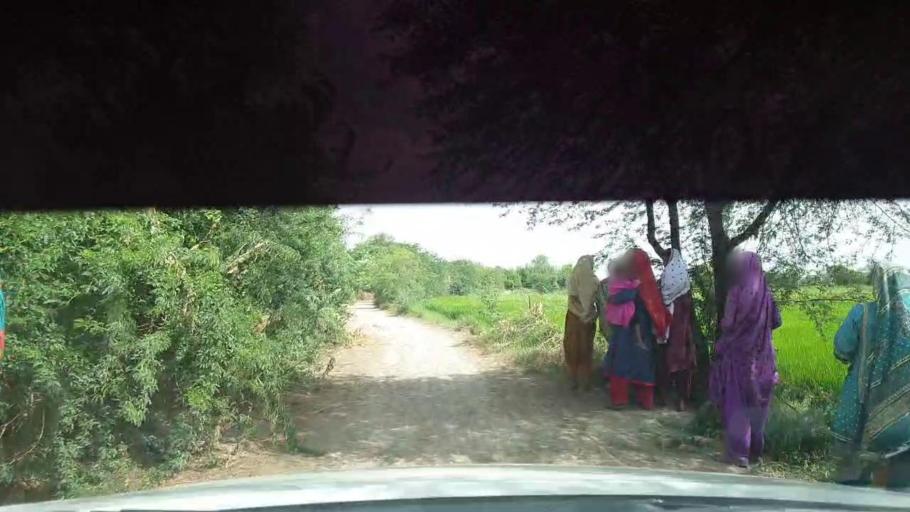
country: PK
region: Sindh
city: Kadhan
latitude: 24.6138
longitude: 69.0259
